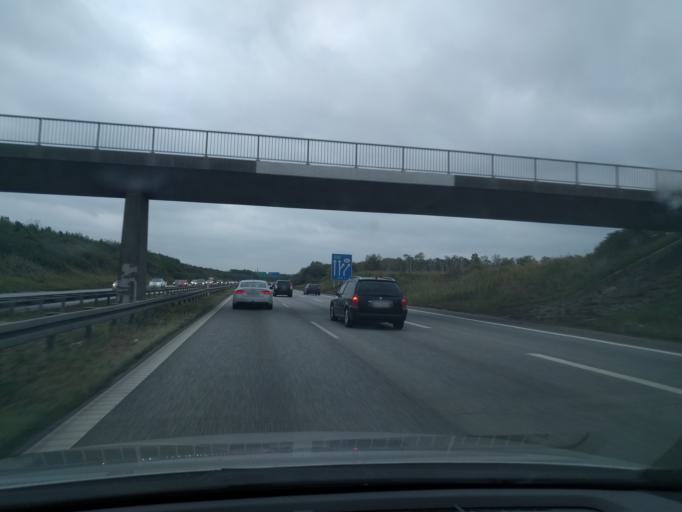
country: DK
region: Capital Region
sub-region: Frederiksberg Kommune
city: Frederiksberg
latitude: 55.6287
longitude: 12.5224
